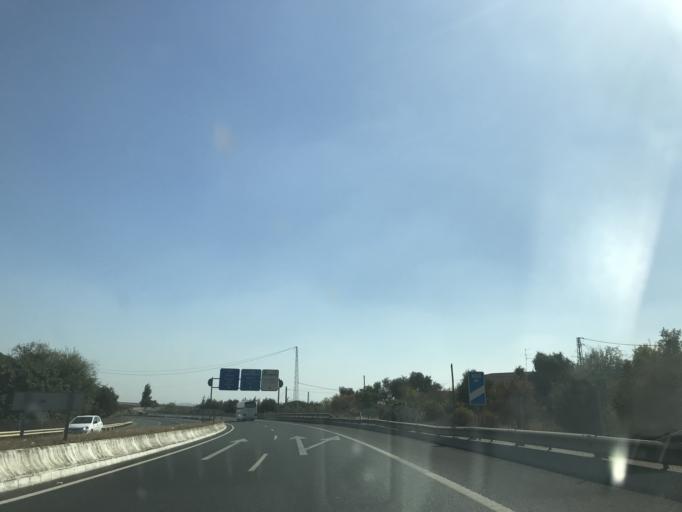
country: ES
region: Andalusia
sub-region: Provincia de Sevilla
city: Alcala de Guadaira
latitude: 37.3315
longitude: -5.8207
